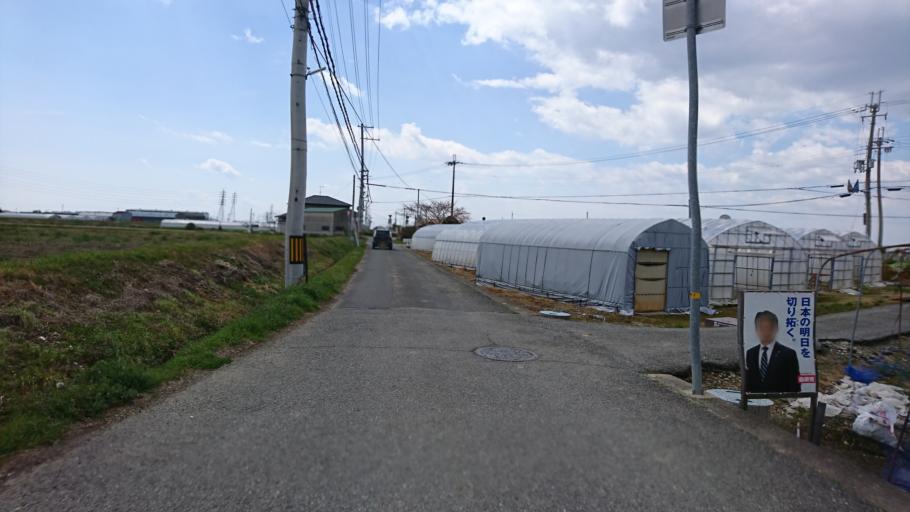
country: JP
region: Hyogo
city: Miki
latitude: 34.7572
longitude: 134.9496
